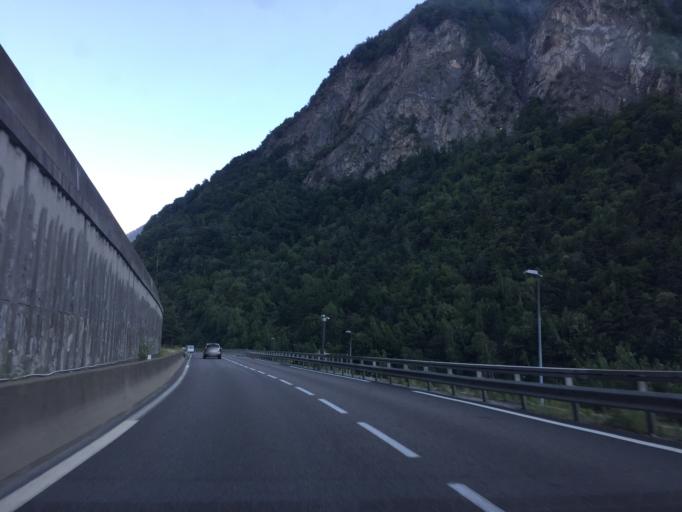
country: FR
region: Rhone-Alpes
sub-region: Departement de la Savoie
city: Moutiers
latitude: 45.4891
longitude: 6.5194
